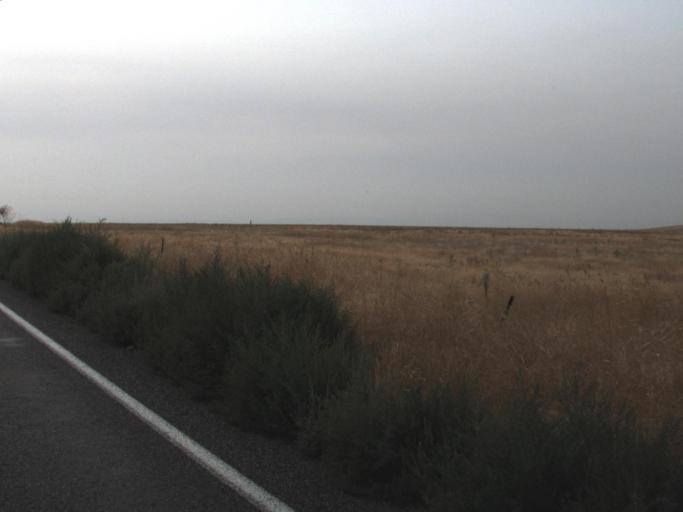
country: US
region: Washington
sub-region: Yakima County
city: Sunnyside
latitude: 46.4132
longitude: -119.9481
